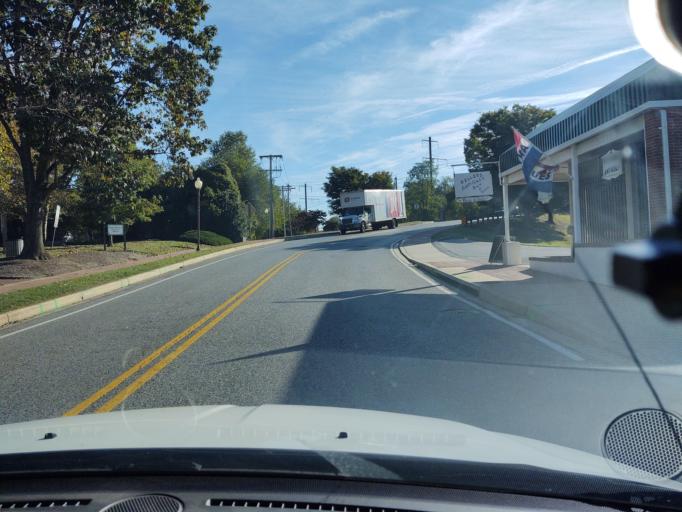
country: US
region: Maryland
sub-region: Prince George's County
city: Glenn Dale
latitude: 39.0083
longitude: -76.7802
